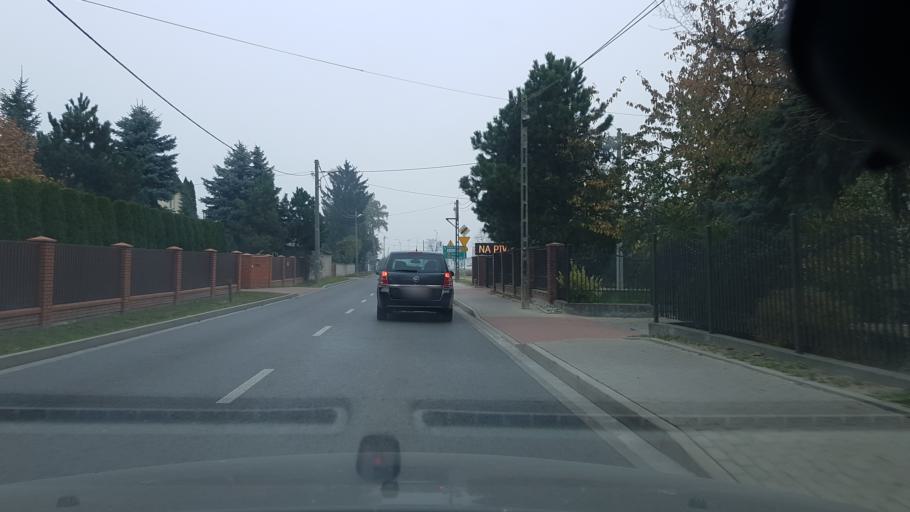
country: PL
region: Masovian Voivodeship
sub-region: Powiat pruszkowski
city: Piastow
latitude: 52.2128
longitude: 20.8398
